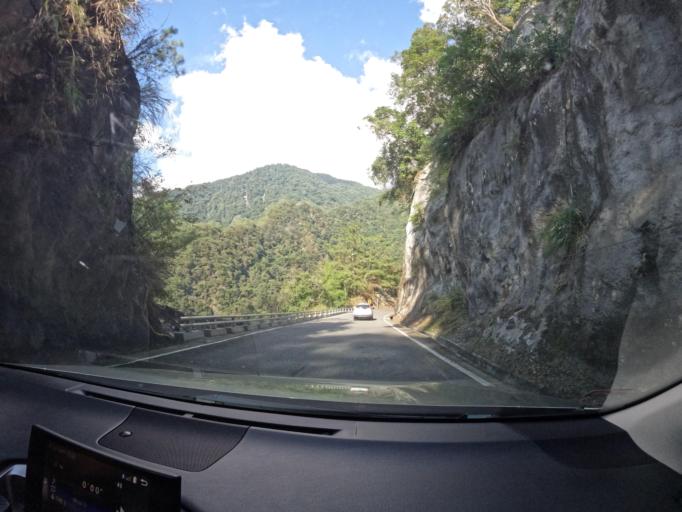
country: TW
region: Taiwan
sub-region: Taitung
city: Taitung
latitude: 23.1813
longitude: 121.0385
